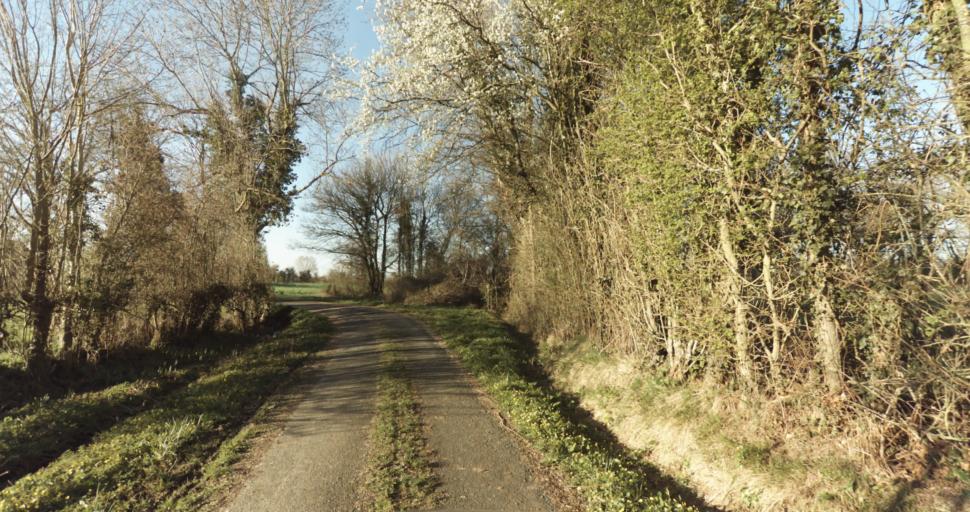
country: FR
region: Lower Normandy
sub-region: Departement de l'Orne
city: Trun
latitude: 48.9106
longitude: 0.0174
